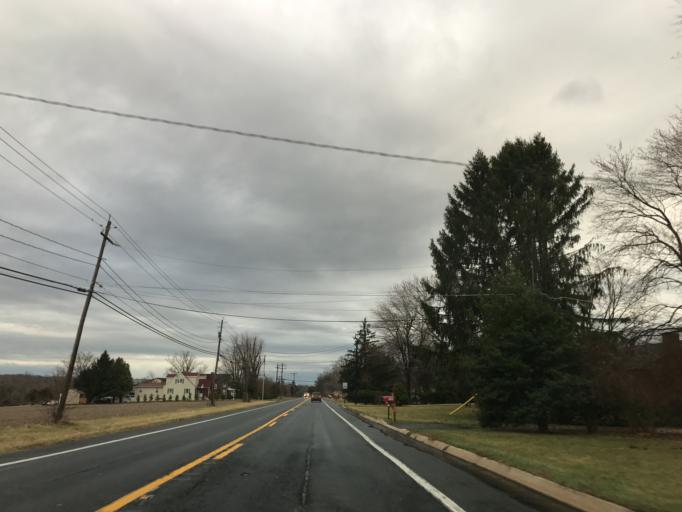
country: US
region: Maryland
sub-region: Harford County
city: Riverside
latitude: 39.5026
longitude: -76.2665
